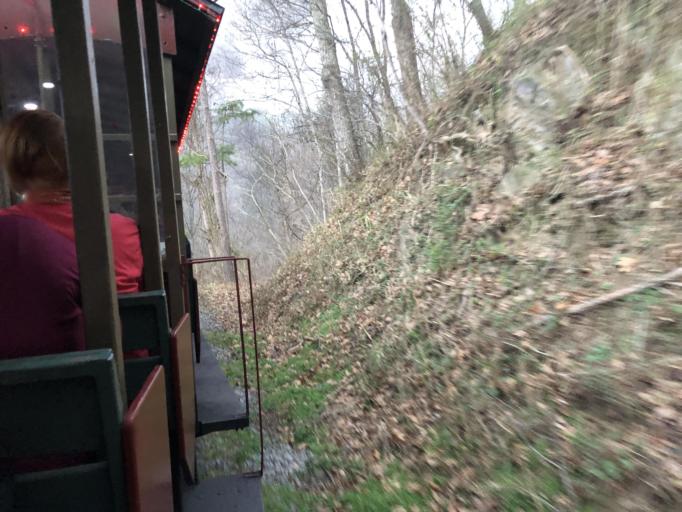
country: US
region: Tennessee
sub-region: Sevier County
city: Pigeon Forge
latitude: 35.7955
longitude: -83.5247
